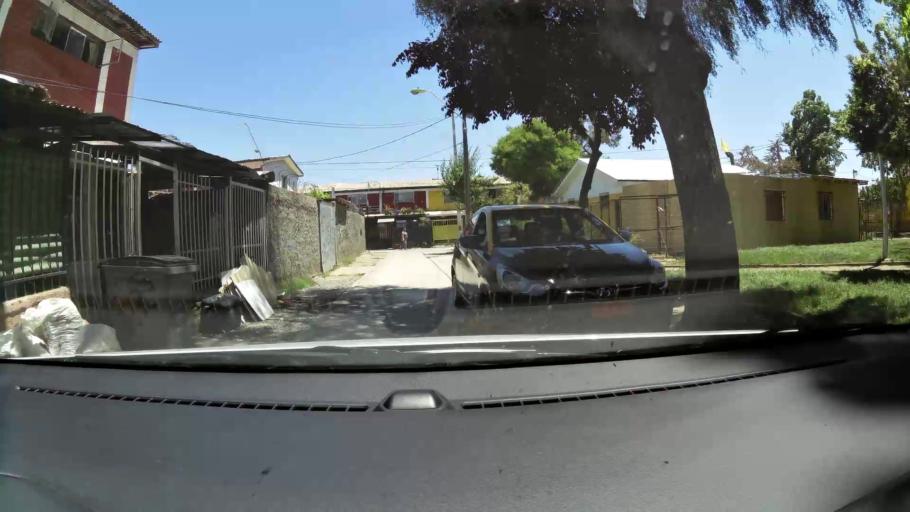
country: CL
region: Santiago Metropolitan
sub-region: Provincia de Santiago
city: La Pintana
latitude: -33.5808
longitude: -70.6669
